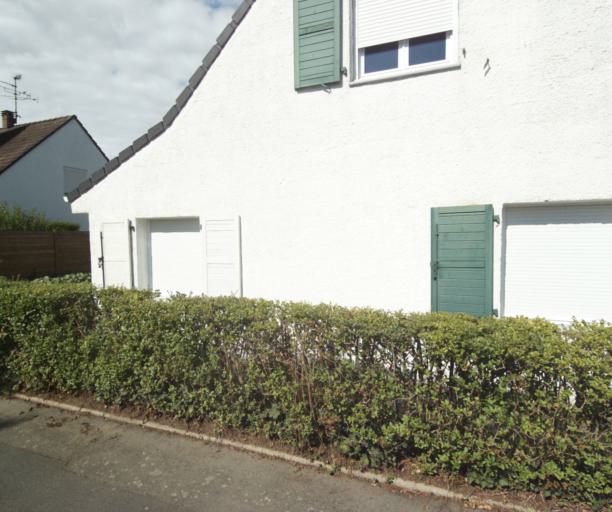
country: FR
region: Nord-Pas-de-Calais
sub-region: Departement du Nord
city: Hem
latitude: 50.6680
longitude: 3.1829
